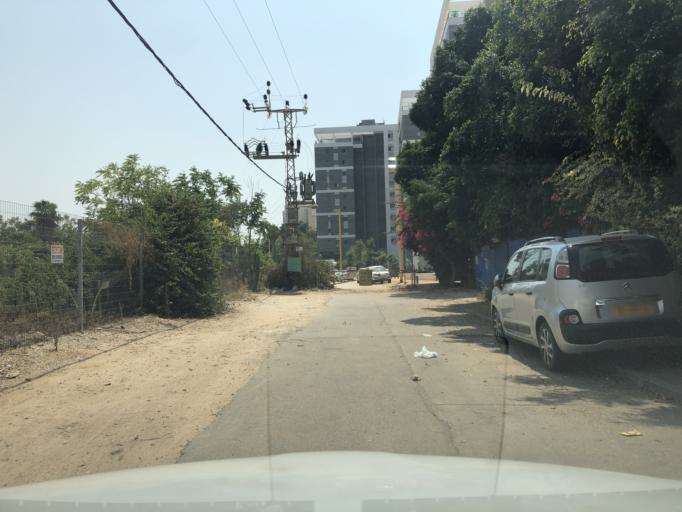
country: IL
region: Central District
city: Ganne Tiqwa
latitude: 32.0661
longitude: 34.8810
